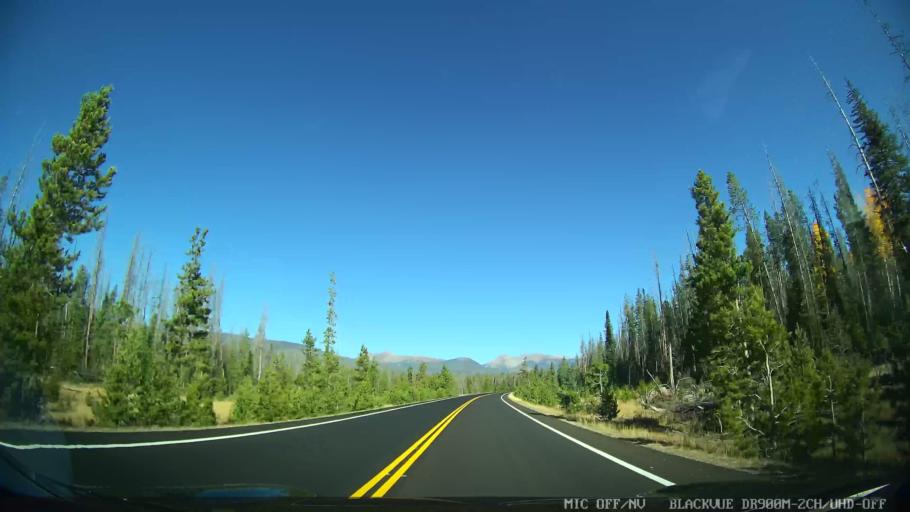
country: US
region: Colorado
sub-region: Grand County
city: Granby
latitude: 40.2848
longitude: -105.8411
